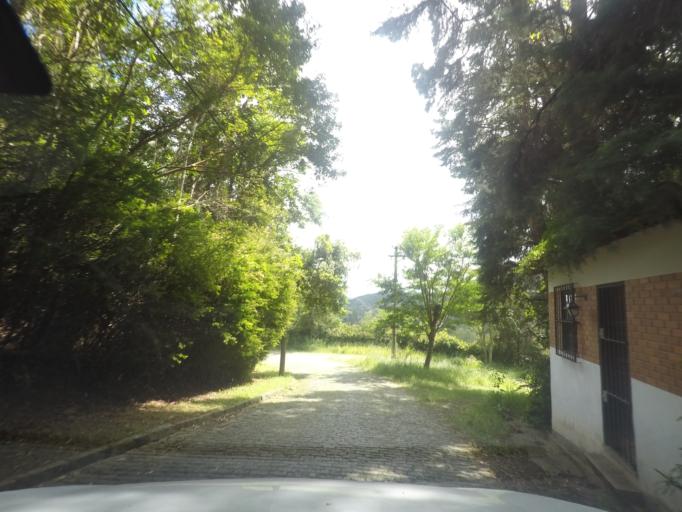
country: BR
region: Rio de Janeiro
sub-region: Teresopolis
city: Teresopolis
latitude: -22.3942
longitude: -42.9880
